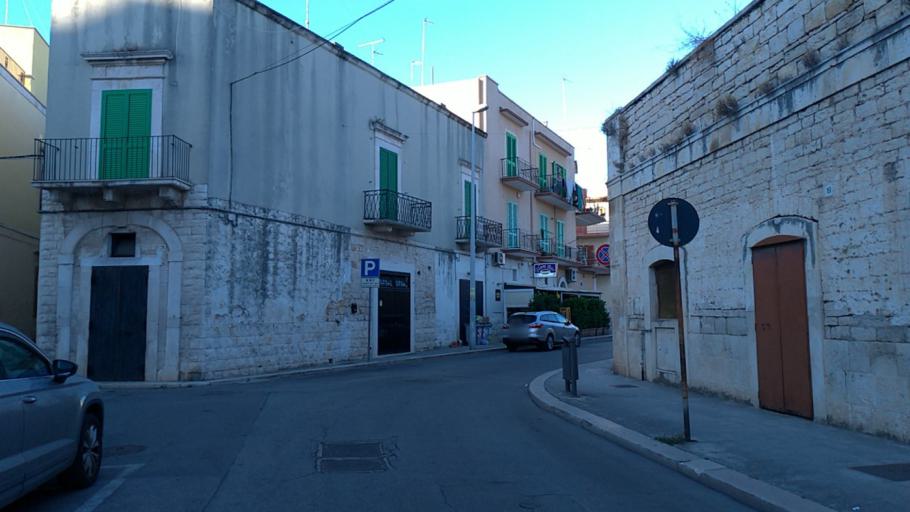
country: IT
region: Apulia
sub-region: Provincia di Bari
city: Giovinazzo
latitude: 41.1861
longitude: 16.6727
